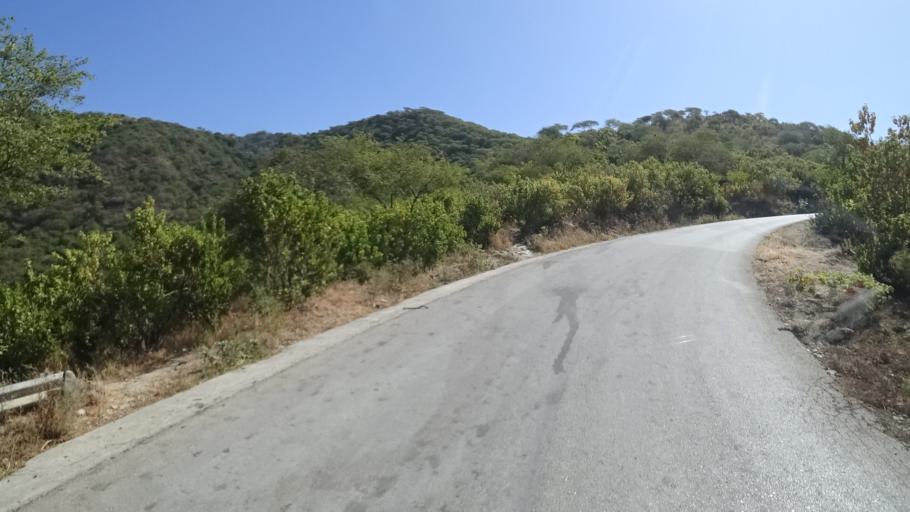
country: OM
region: Zufar
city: Salalah
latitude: 17.0751
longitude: 54.4395
